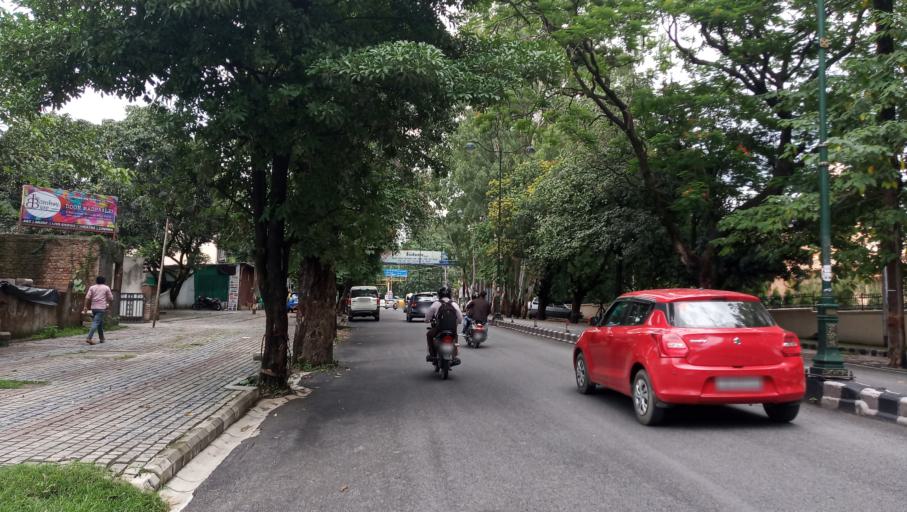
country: IN
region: Uttarakhand
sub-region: Dehradun
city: Raipur
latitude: 30.3704
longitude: 78.0762
